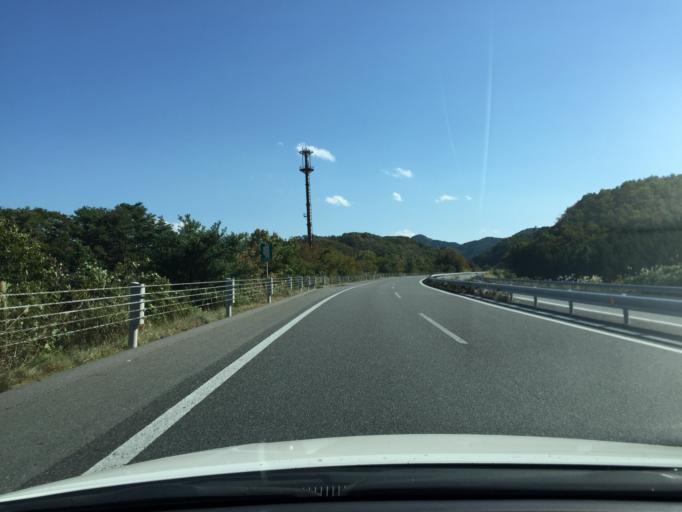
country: JP
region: Fukushima
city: Iwaki
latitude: 37.1427
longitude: 140.7470
